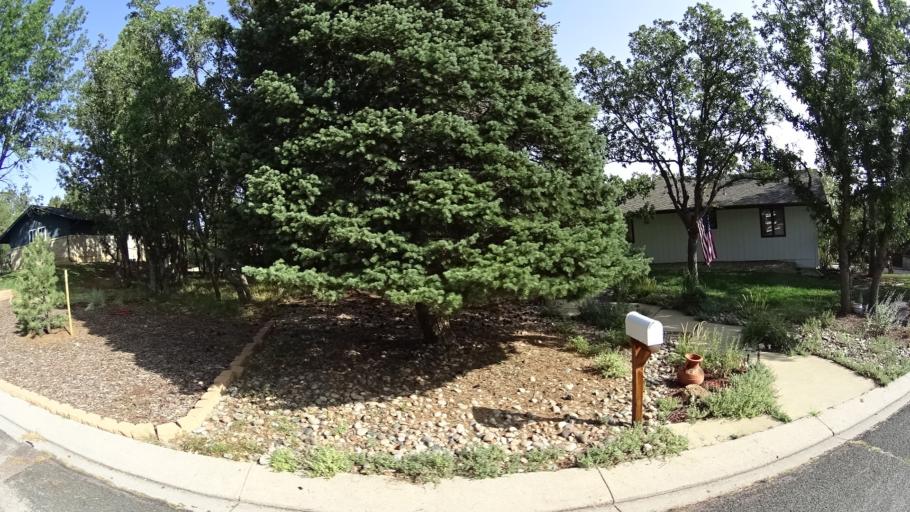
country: US
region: Colorado
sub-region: El Paso County
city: Colorado Springs
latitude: 38.8179
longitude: -104.8686
